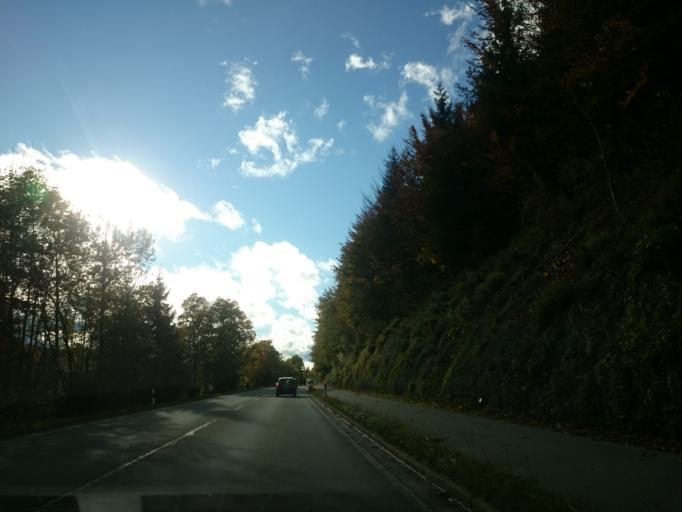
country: DE
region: Bavaria
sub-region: Upper Bavaria
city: Farchant
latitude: 47.4886
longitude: 11.1641
